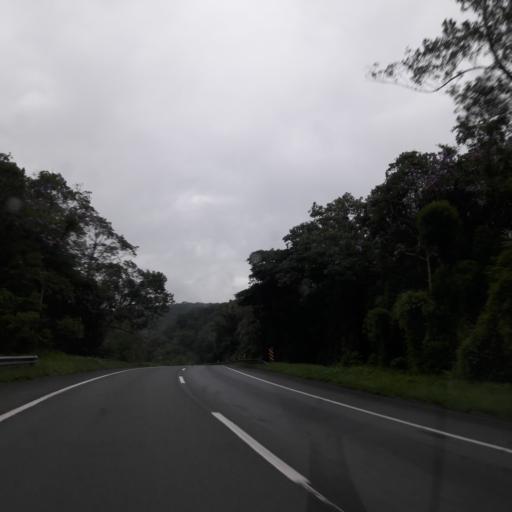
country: BR
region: Sao Paulo
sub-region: Cajati
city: Cajati
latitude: -24.9668
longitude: -48.4488
